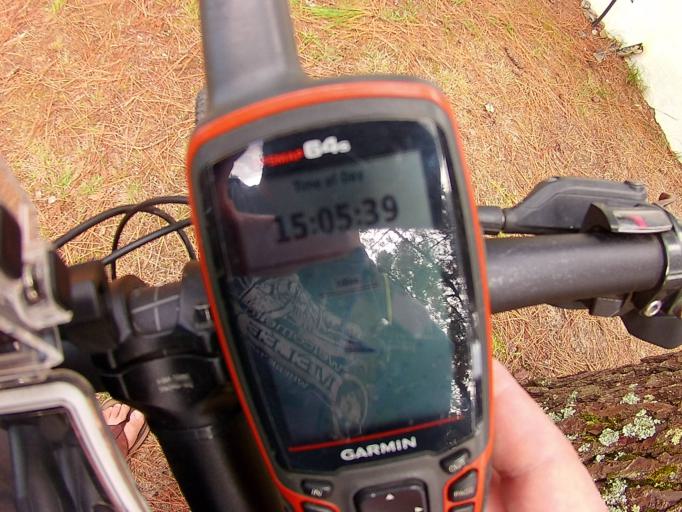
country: FR
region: Aquitaine
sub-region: Departement des Landes
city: Labenne
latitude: 43.6033
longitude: -1.4559
